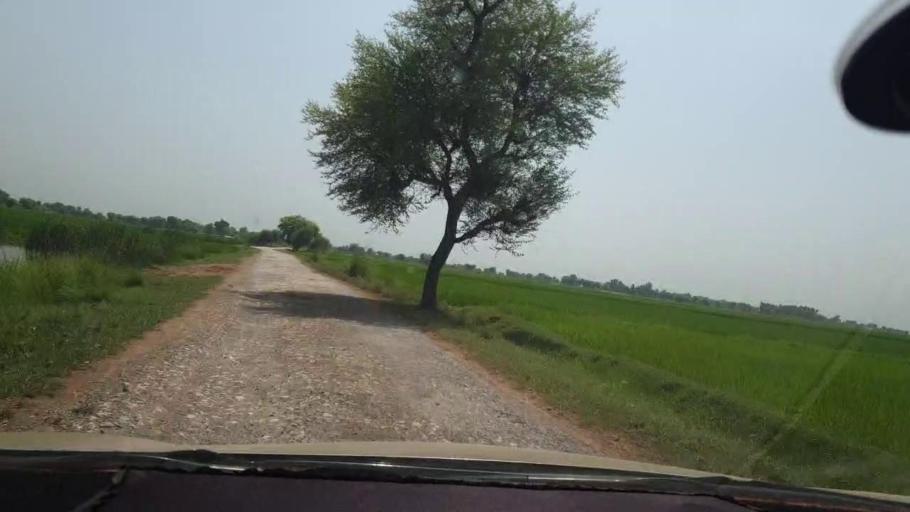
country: PK
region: Sindh
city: Kambar
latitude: 27.6436
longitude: 67.9320
